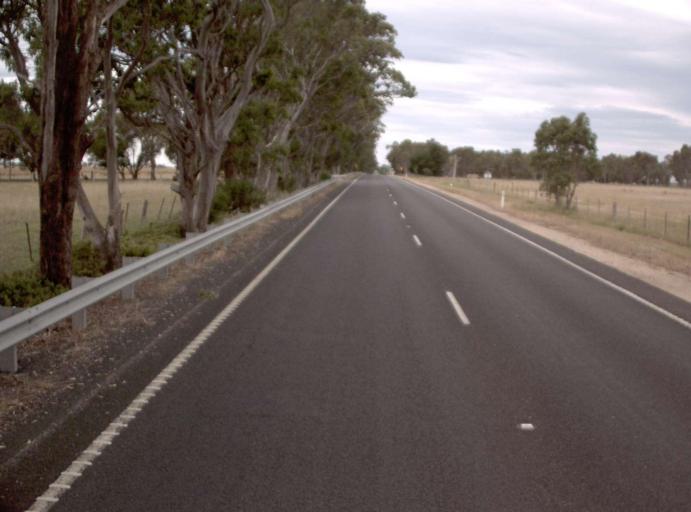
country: AU
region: Victoria
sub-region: East Gippsland
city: Bairnsdale
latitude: -37.9048
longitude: 147.7015
